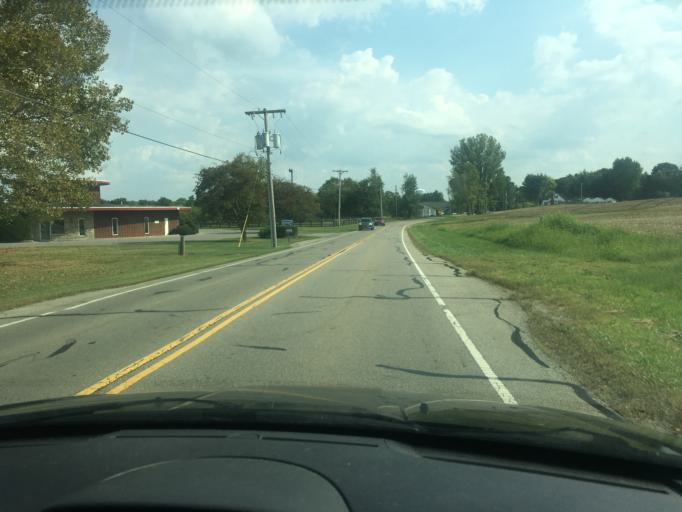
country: US
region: Ohio
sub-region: Champaign County
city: Urbana
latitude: 40.1213
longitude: -83.7656
